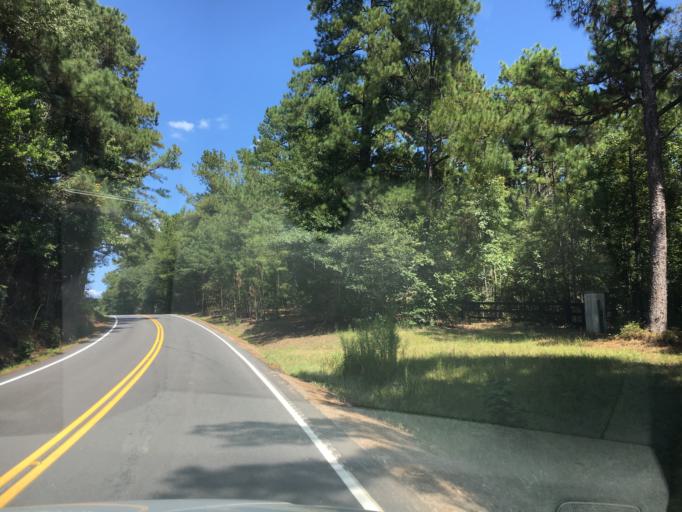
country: US
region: South Carolina
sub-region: Aiken County
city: New Ellenton
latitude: 33.5022
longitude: -81.6553
